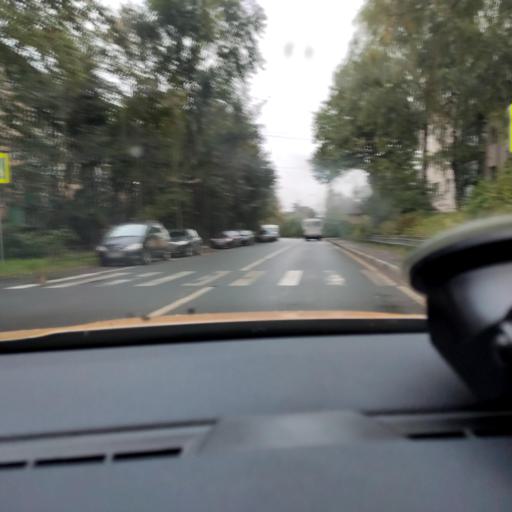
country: RU
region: Moskovskaya
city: Druzhba
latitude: 55.8852
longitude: 37.7544
